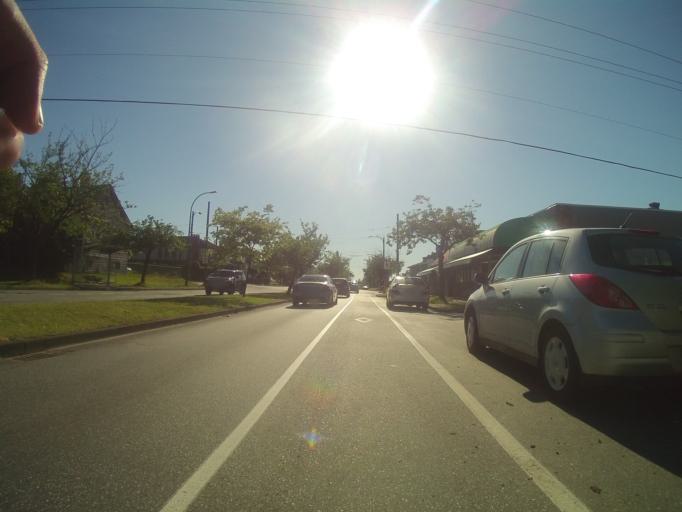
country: CA
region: British Columbia
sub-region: Fraser Valley Regional District
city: North Vancouver
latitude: 49.2507
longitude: -123.0489
